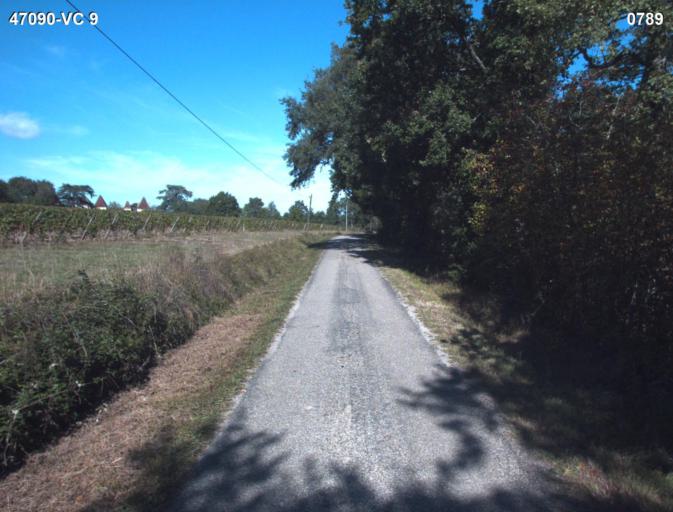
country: FR
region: Aquitaine
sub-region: Departement du Lot-et-Garonne
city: Nerac
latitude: 44.1802
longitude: 0.3873
